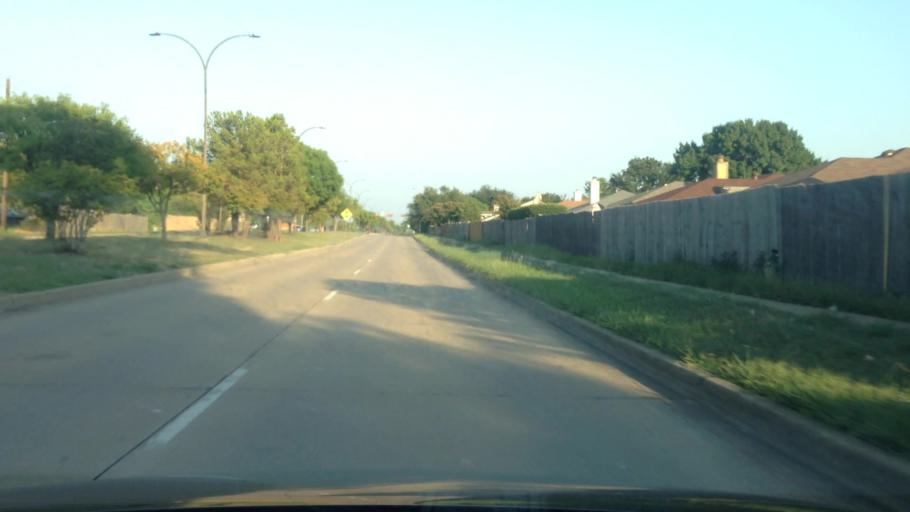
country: US
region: Texas
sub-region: Tarrant County
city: Dalworthington Gardens
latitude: 32.6587
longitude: -97.1096
